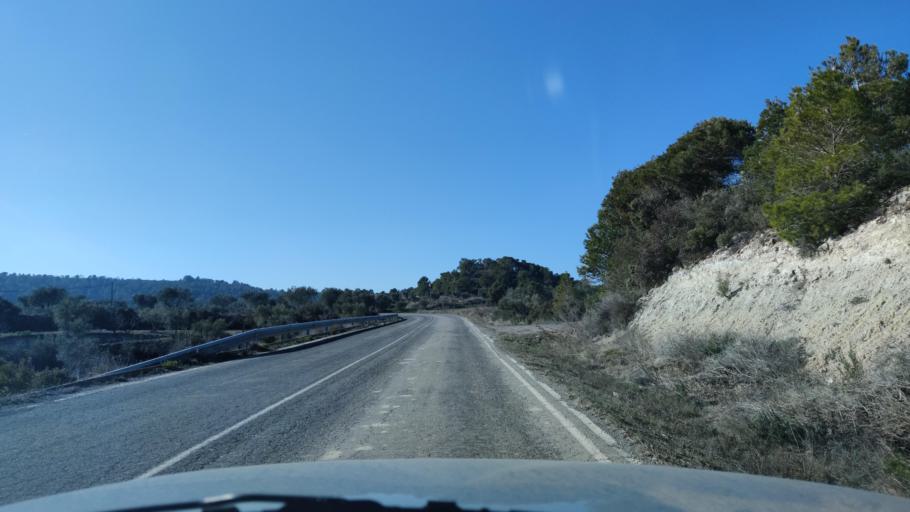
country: ES
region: Catalonia
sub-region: Provincia de Lleida
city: Maials
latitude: 41.3298
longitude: 0.4317
